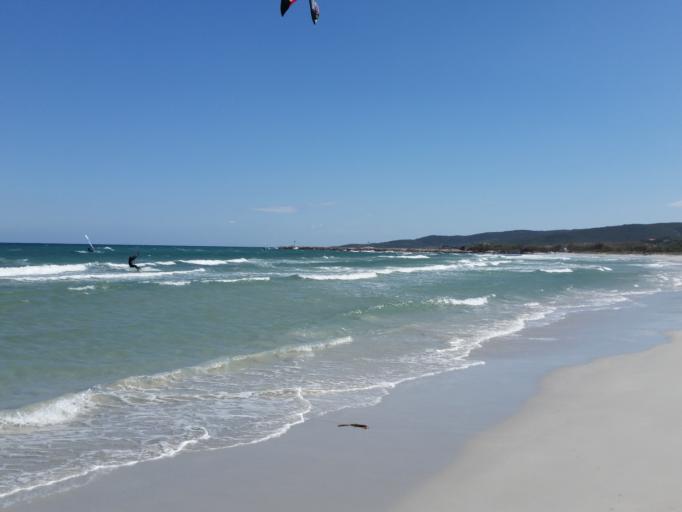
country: IT
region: Sardinia
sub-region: Provincia di Olbia-Tempio
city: San Teodoro
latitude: 40.7855
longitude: 9.6712
